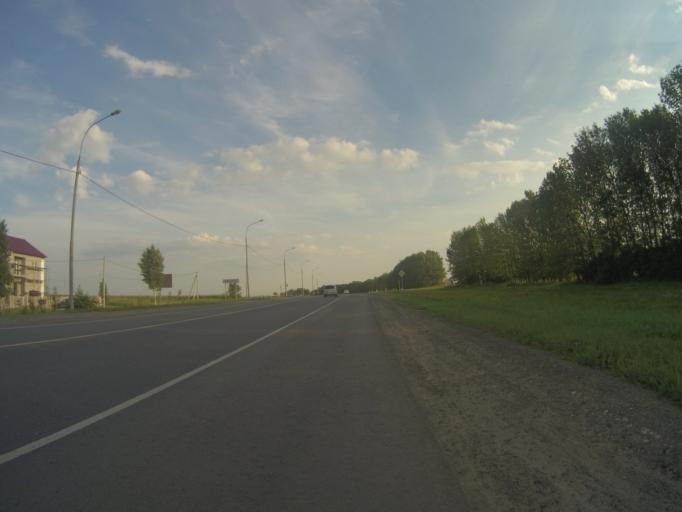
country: RU
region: Vladimir
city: Suzdal'
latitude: 56.3134
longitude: 40.4714
